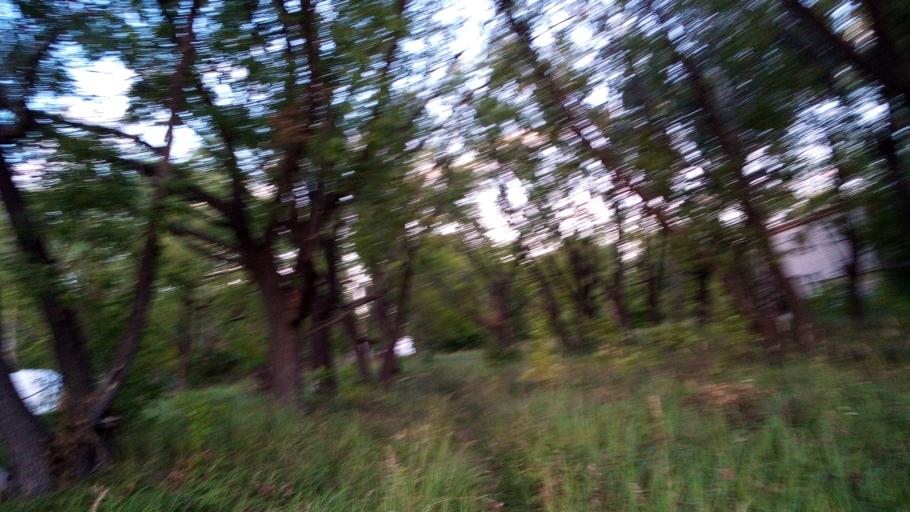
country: RU
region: Chelyabinsk
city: Potanino
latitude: 55.2899
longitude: 61.5117
